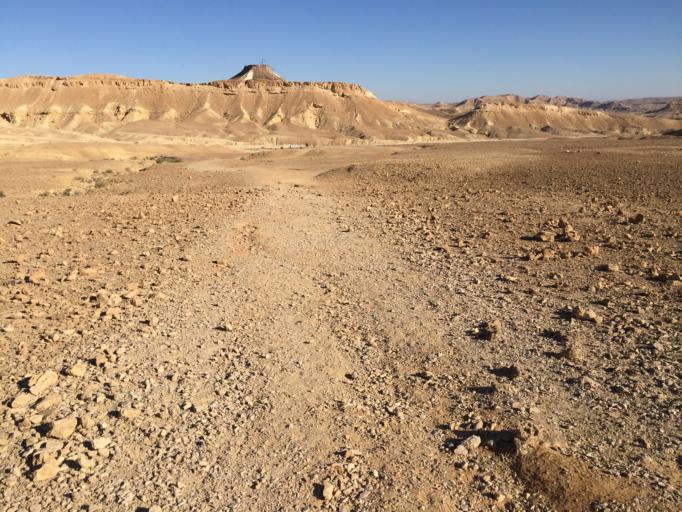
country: IL
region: Southern District
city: Mitzpe Ramon
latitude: 30.5769
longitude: 34.8808
